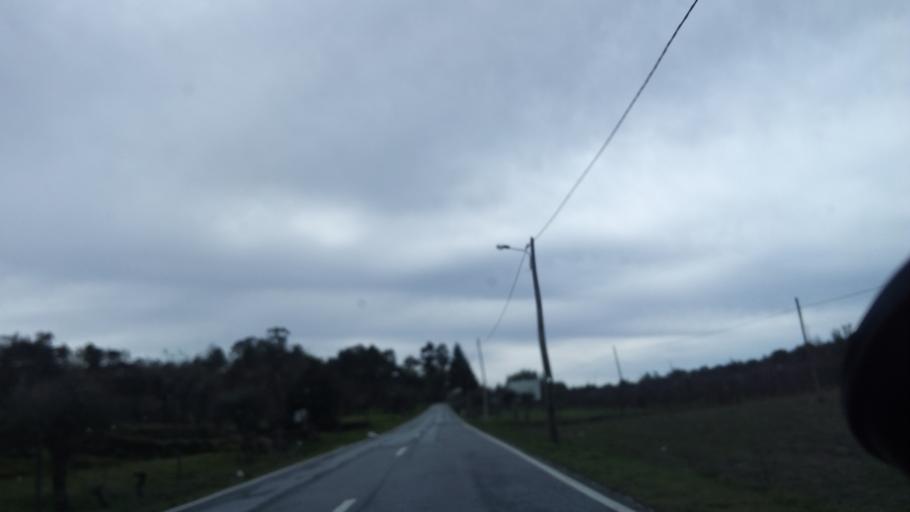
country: PT
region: Guarda
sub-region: Seia
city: Seia
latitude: 40.4835
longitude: -7.6637
